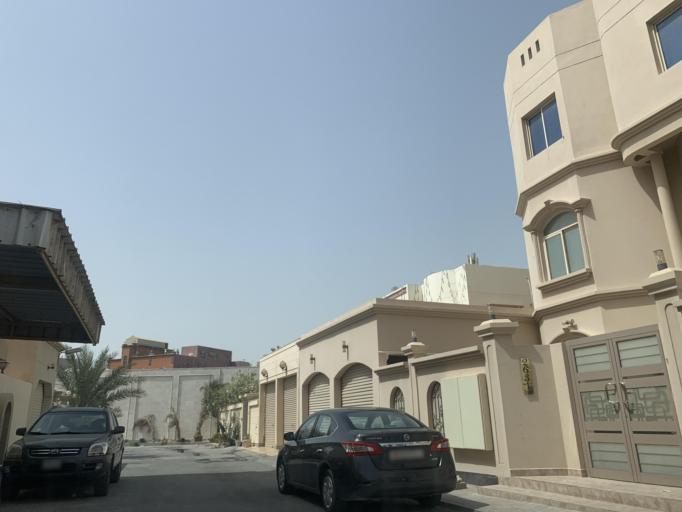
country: BH
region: Northern
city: Madinat `Isa
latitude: 26.1766
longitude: 50.5606
